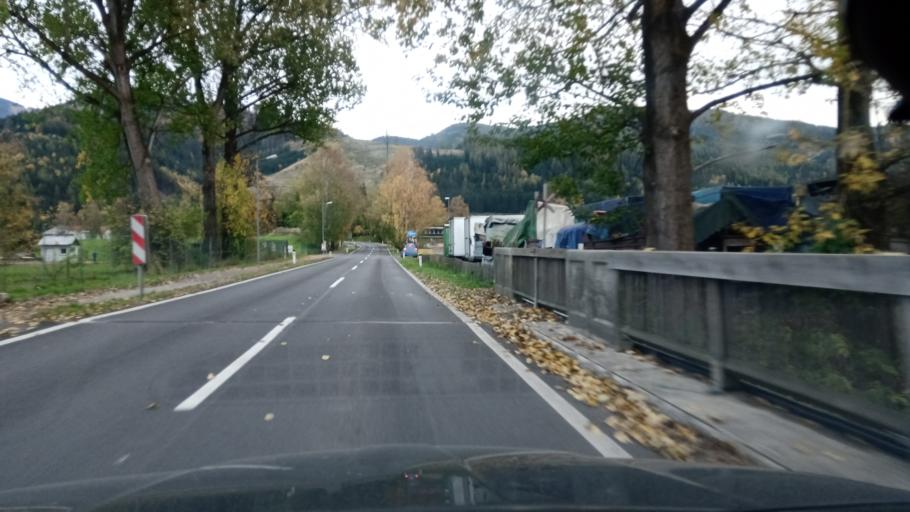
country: AT
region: Styria
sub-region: Politischer Bezirk Leoben
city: Niklasdorf
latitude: 47.3967
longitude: 15.1480
